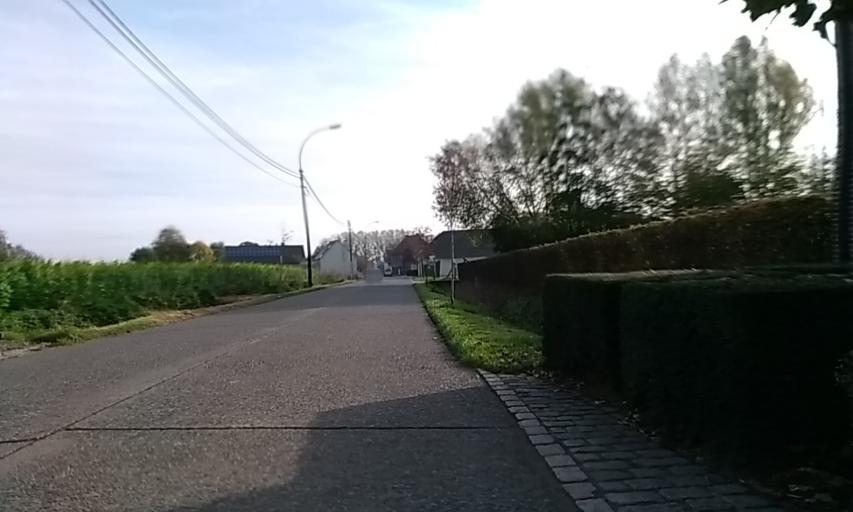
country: BE
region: Flanders
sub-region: Provincie Oost-Vlaanderen
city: Oosterzele
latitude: 50.9292
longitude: 3.8231
